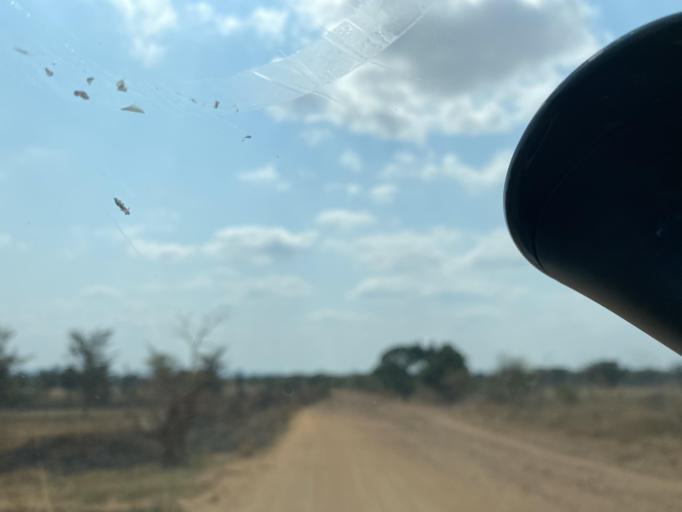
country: ZM
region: Lusaka
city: Chongwe
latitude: -15.5879
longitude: 28.7687
